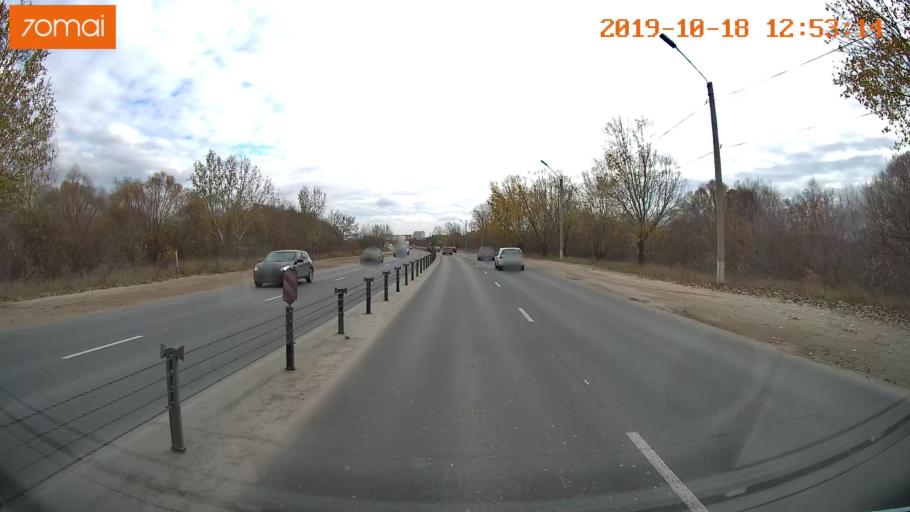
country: RU
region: Rjazan
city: Ryazan'
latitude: 54.6459
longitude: 39.7037
